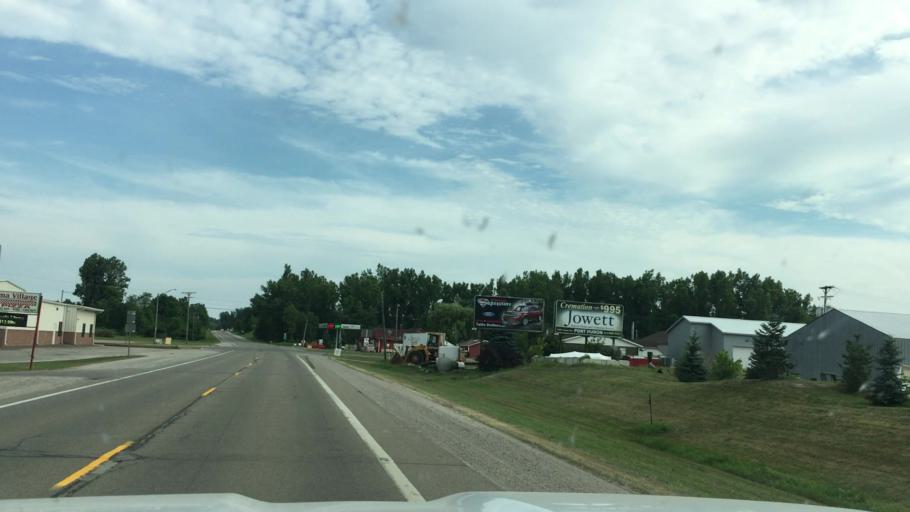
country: US
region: Michigan
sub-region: Sanilac County
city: Brown City
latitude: 43.1540
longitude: -83.0753
